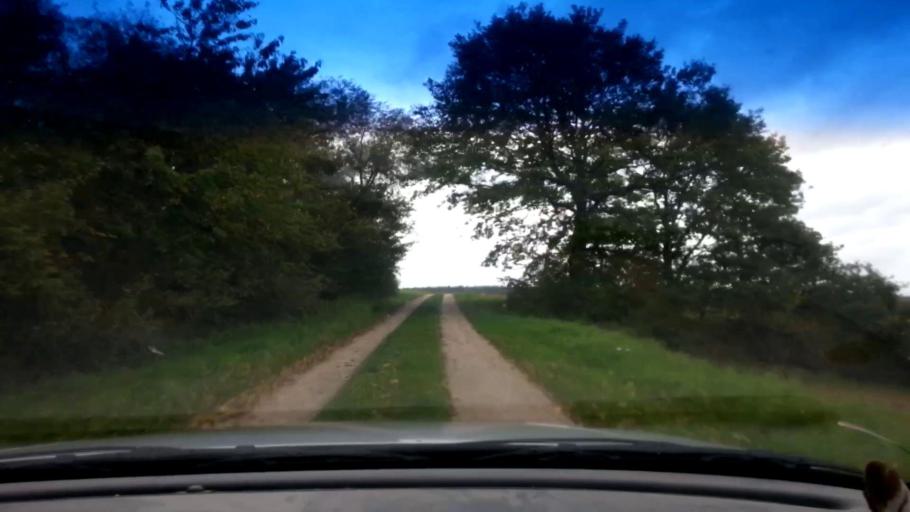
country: DE
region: Bavaria
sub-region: Regierungsbezirk Unterfranken
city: Kirchlauter
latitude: 50.0363
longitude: 10.7374
